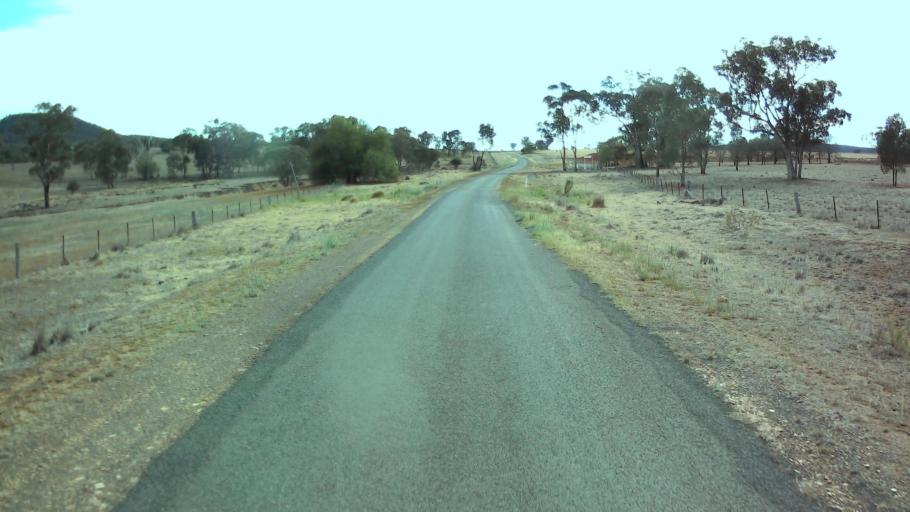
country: AU
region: New South Wales
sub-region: Weddin
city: Grenfell
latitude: -33.8399
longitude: 148.2641
